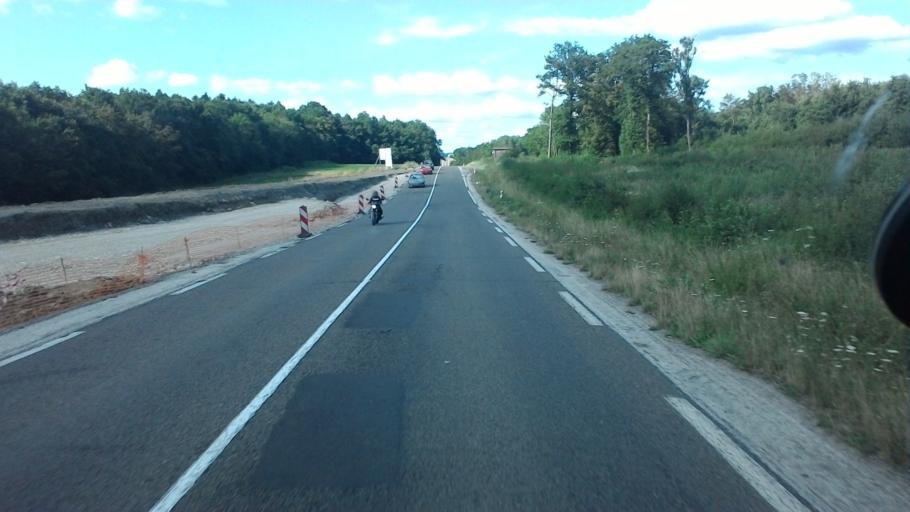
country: FR
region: Franche-Comte
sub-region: Departement de la Haute-Saone
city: Luxeuil-les-Bains
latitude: 47.7069
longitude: 6.2934
